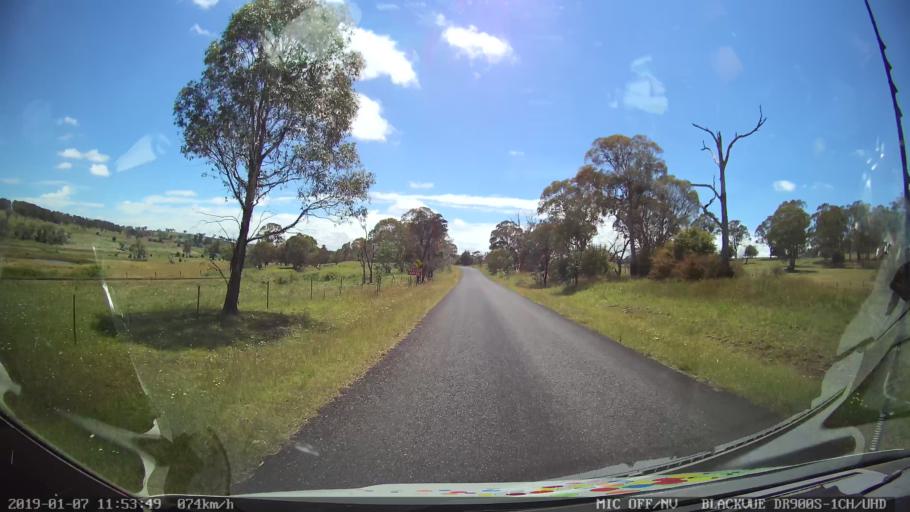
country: AU
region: New South Wales
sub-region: Guyra
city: Guyra
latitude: -30.3020
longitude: 151.6614
